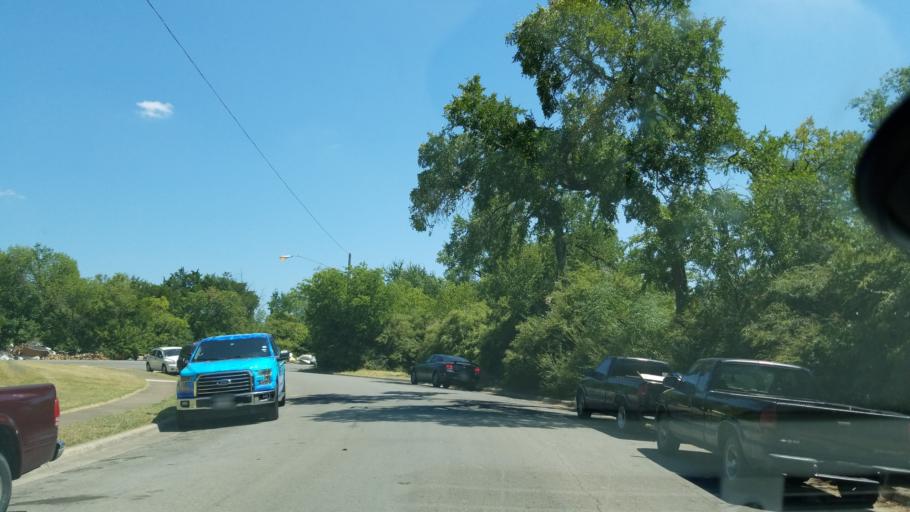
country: US
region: Texas
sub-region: Dallas County
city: Cockrell Hill
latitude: 32.7138
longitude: -96.8878
